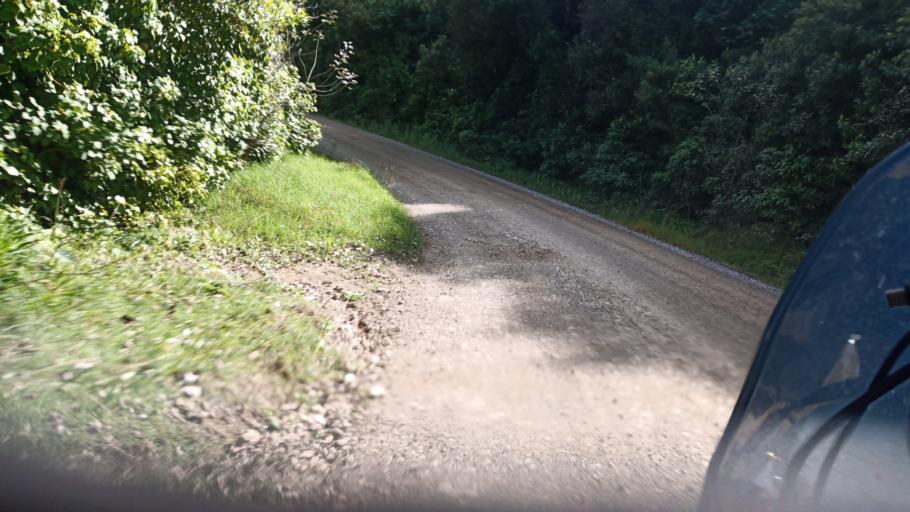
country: NZ
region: Gisborne
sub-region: Gisborne District
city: Gisborne
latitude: -38.4136
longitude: 177.6925
